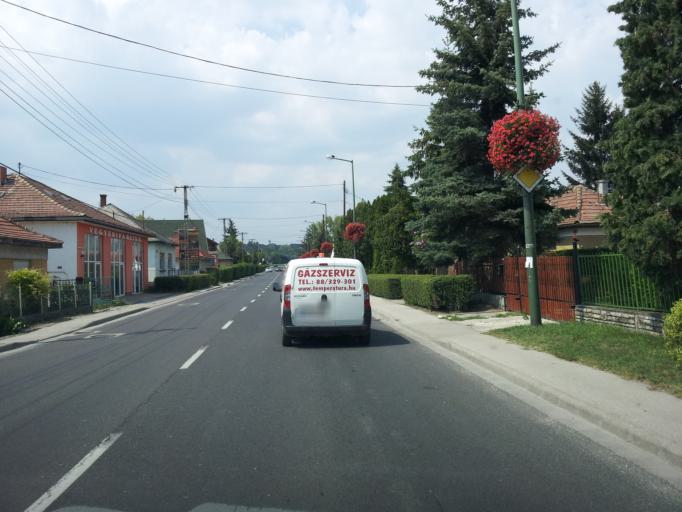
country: HU
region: Veszprem
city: Balatonalmadi
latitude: 47.0659
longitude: 18.0376
